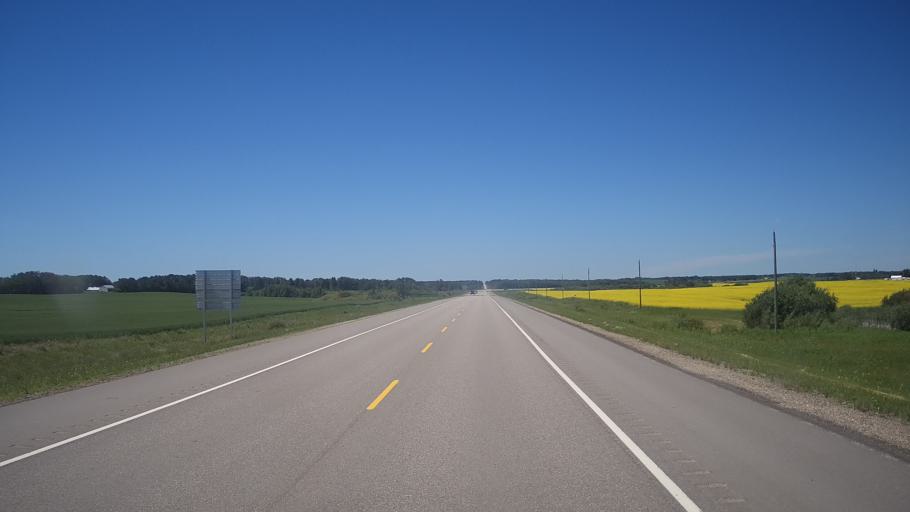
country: CA
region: Manitoba
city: Minnedosa
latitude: 50.2699
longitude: -99.9204
